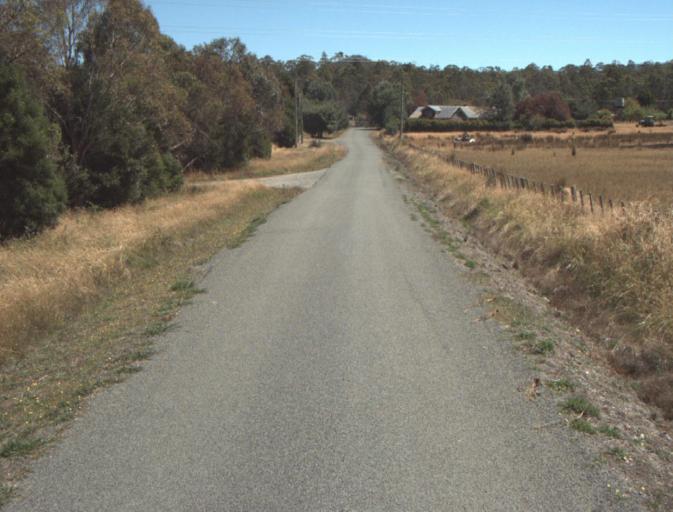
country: AU
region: Tasmania
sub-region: Launceston
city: Newstead
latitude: -41.3919
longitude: 147.3034
